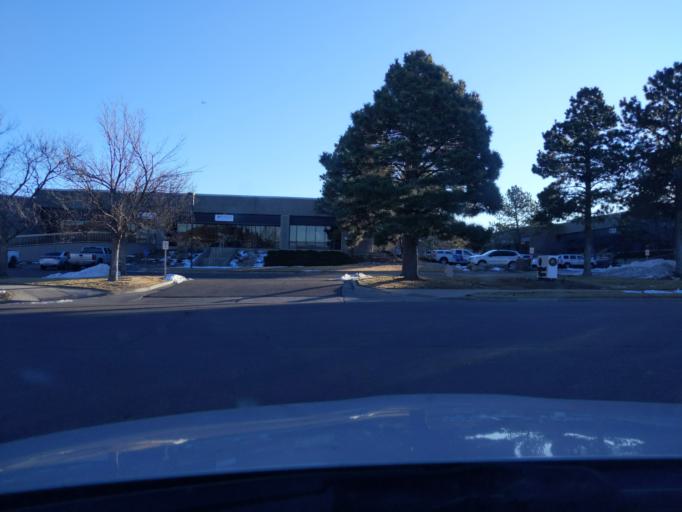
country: US
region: Colorado
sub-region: Arapahoe County
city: Centennial
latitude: 39.5682
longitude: -104.8830
